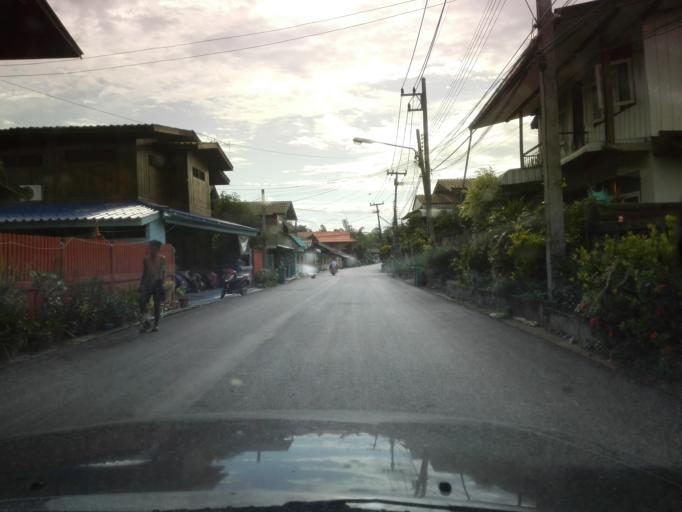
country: TH
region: Tak
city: Mae Ramat
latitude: 16.9820
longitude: 98.5161
